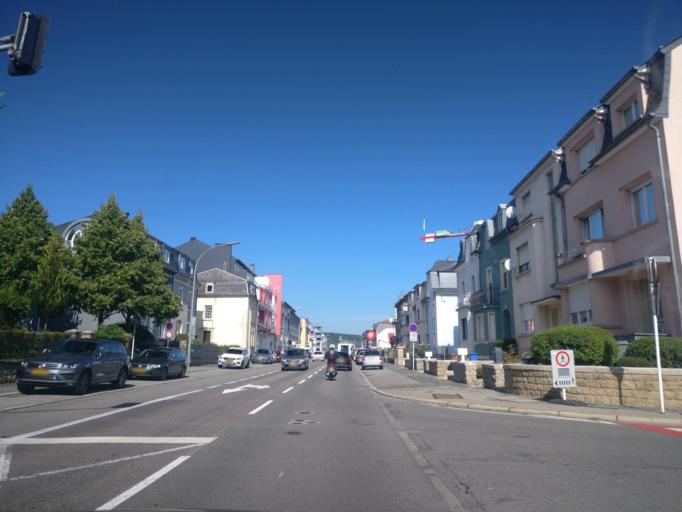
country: LU
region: Luxembourg
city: Bereldange
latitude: 49.6438
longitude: 6.1294
